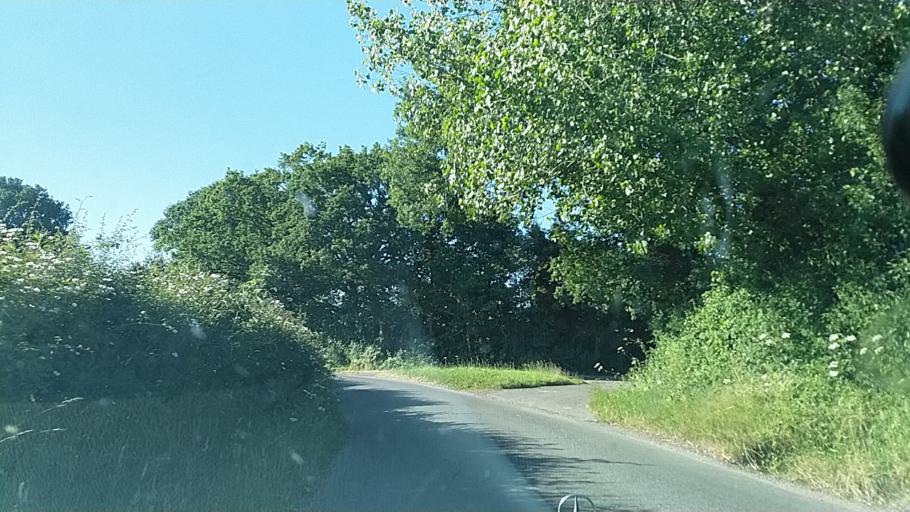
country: GB
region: England
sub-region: Warwickshire
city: Wroxall
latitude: 52.3225
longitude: -1.6448
